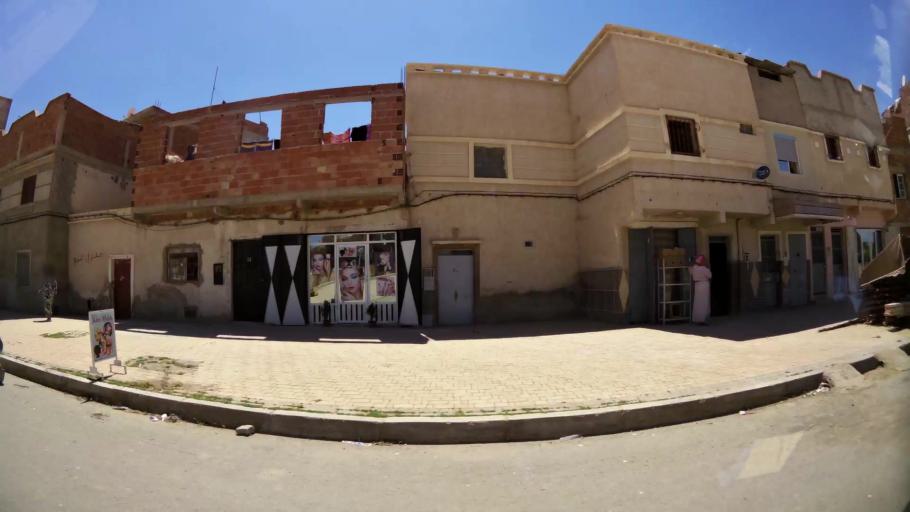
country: MA
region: Oriental
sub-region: Oujda-Angad
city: Oujda
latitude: 34.6566
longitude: -1.9208
